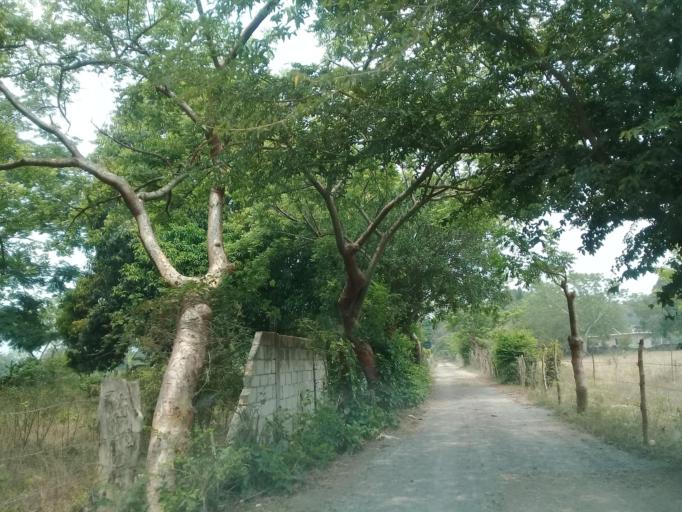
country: MX
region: Veracruz
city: Jamapa
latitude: 18.9584
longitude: -96.1946
